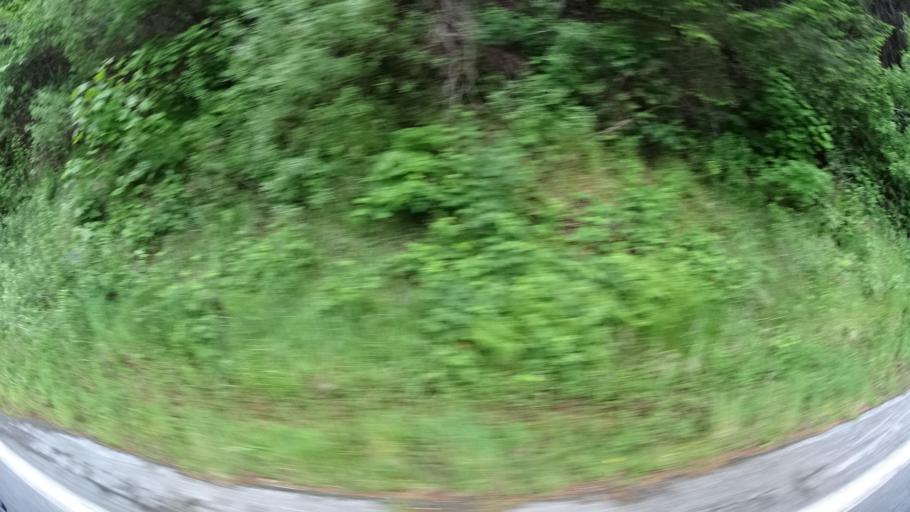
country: US
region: California
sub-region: Humboldt County
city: Willow Creek
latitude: 41.2714
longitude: -123.6068
